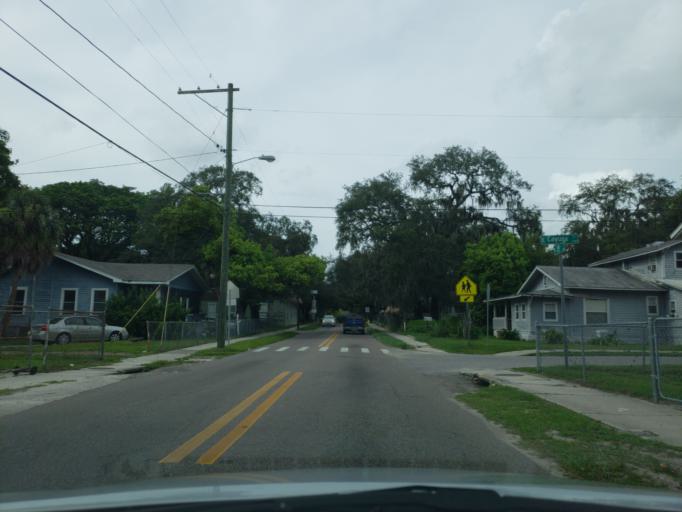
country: US
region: Florida
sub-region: Hillsborough County
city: Tampa
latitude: 27.9868
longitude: -82.4430
